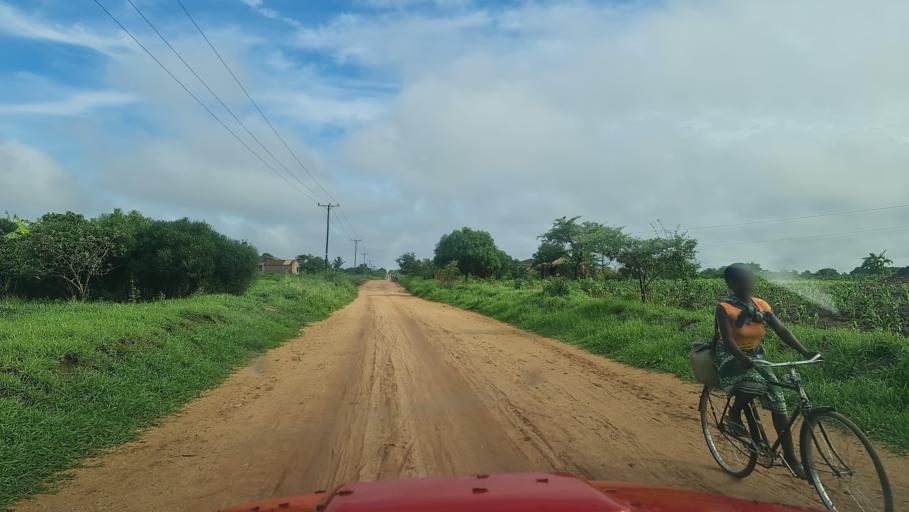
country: MW
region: Southern Region
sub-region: Nsanje District
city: Nsanje
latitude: -17.3131
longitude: 35.5925
